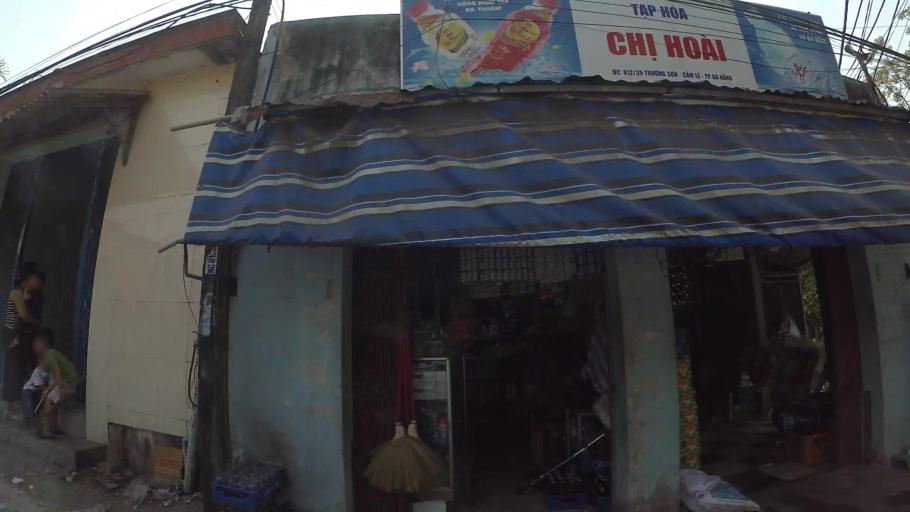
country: VN
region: Da Nang
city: Cam Le
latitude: 16.0131
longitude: 108.1854
